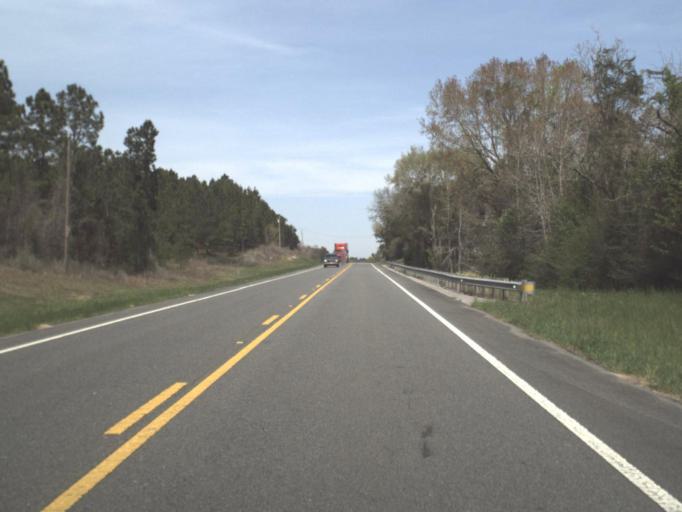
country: US
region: Florida
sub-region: Walton County
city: DeFuniak Springs
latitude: 30.8109
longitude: -85.9583
